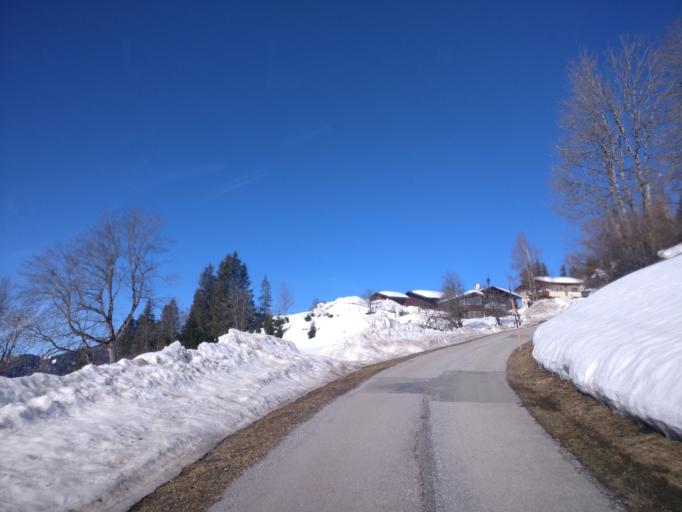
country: AT
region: Salzburg
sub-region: Politischer Bezirk Sankt Johann im Pongau
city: Sankt Johann im Pongau
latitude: 47.3376
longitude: 13.2262
